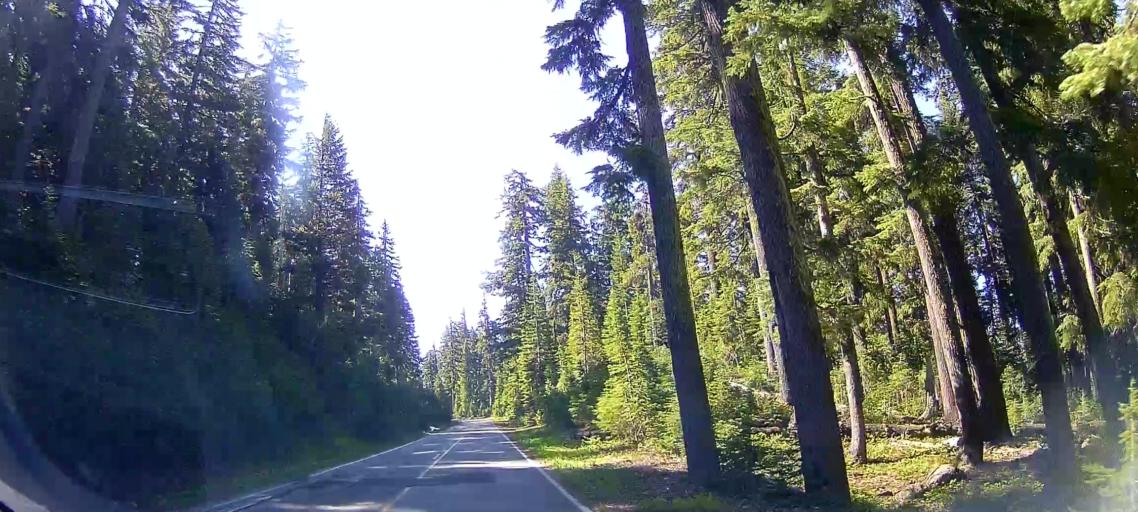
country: US
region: Oregon
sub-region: Jackson County
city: Shady Cove
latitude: 42.8838
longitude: -122.1294
